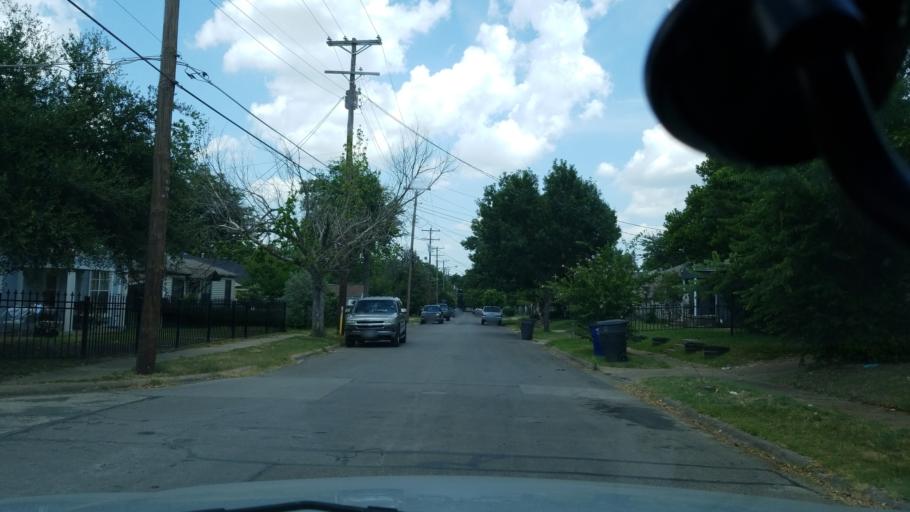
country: US
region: Texas
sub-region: Dallas County
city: Cockrell Hill
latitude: 32.7311
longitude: -96.8816
